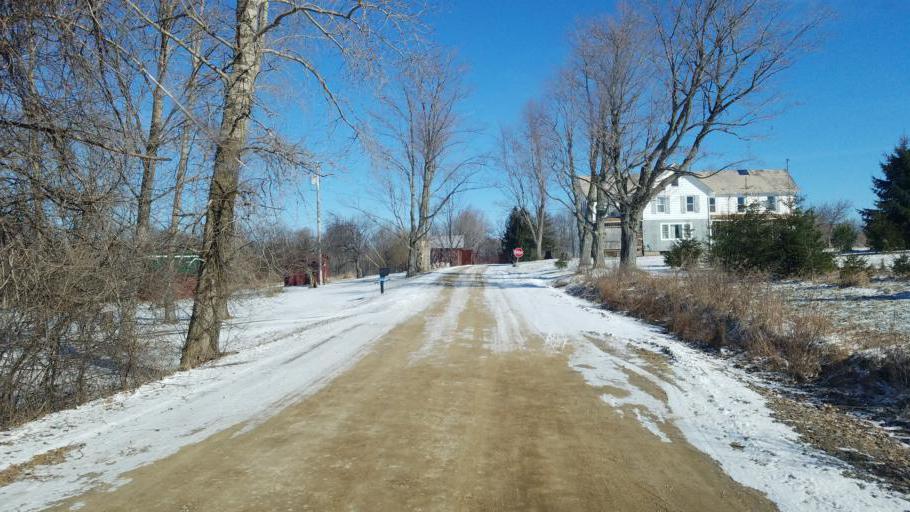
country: US
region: New York
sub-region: Allegany County
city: Wellsville
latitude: 42.1569
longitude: -77.9462
